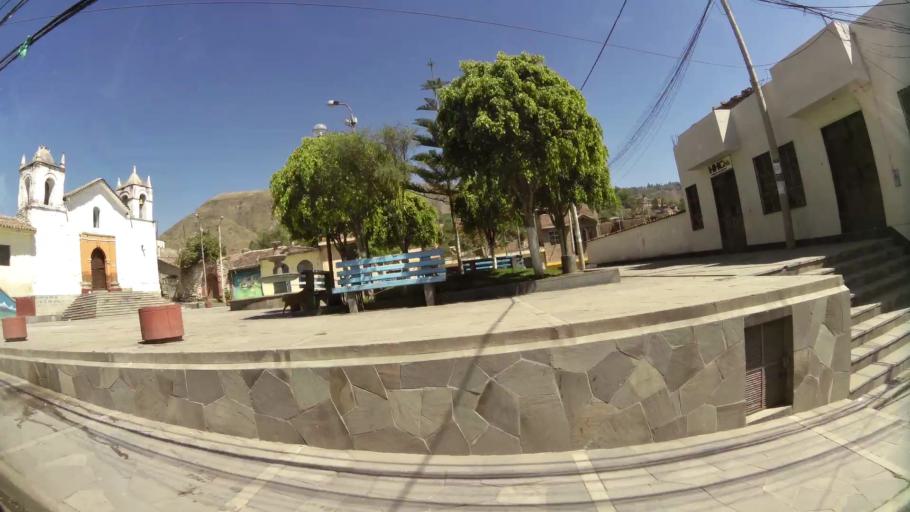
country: PE
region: Ayacucho
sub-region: Provincia de Huamanga
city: Carmen Alto
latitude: -13.1756
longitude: -74.2262
